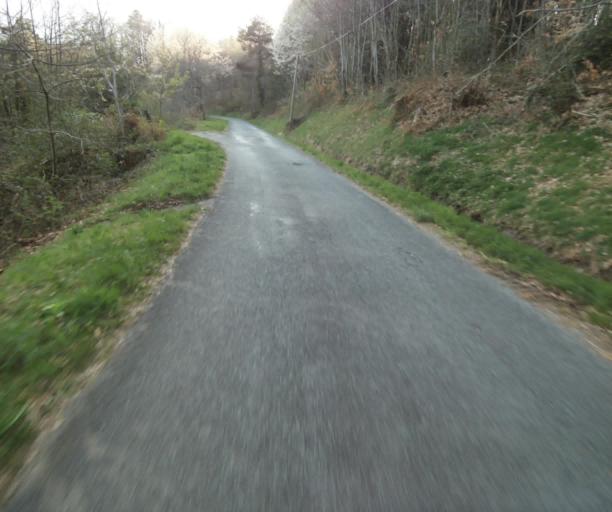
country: FR
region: Limousin
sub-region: Departement de la Correze
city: Correze
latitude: 45.3834
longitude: 1.8438
